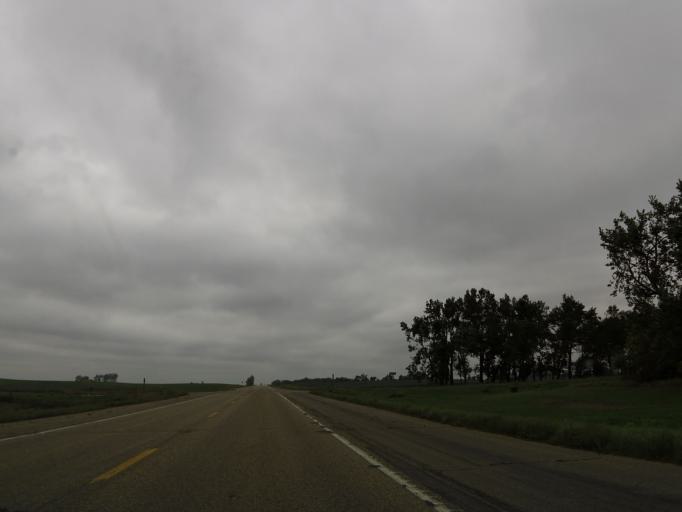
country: US
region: South Dakota
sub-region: Deuel County
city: Clear Lake
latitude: 44.9332
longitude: -96.6175
